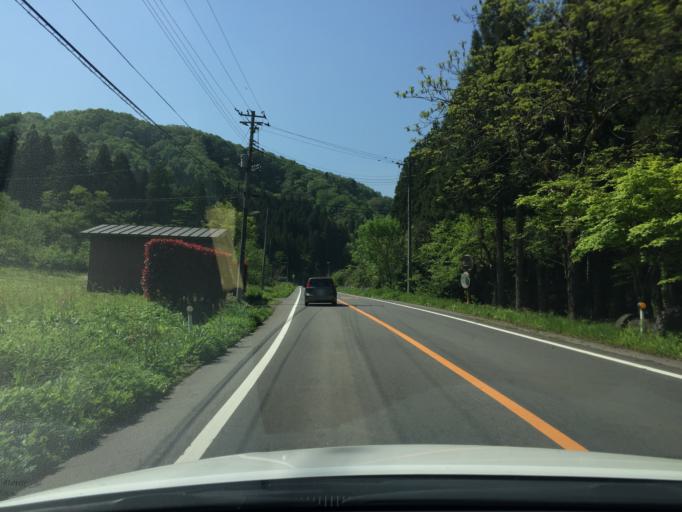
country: JP
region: Niigata
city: Muramatsu
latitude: 37.6554
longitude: 139.1366
